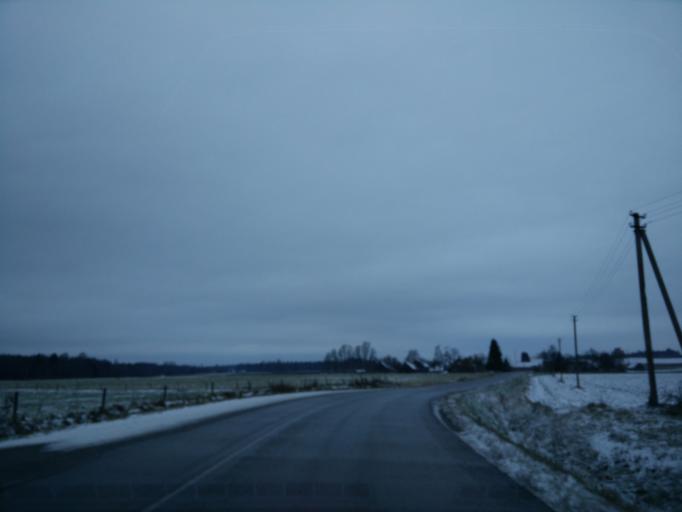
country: LT
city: Tytuveneliai
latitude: 55.5110
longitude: 23.2838
